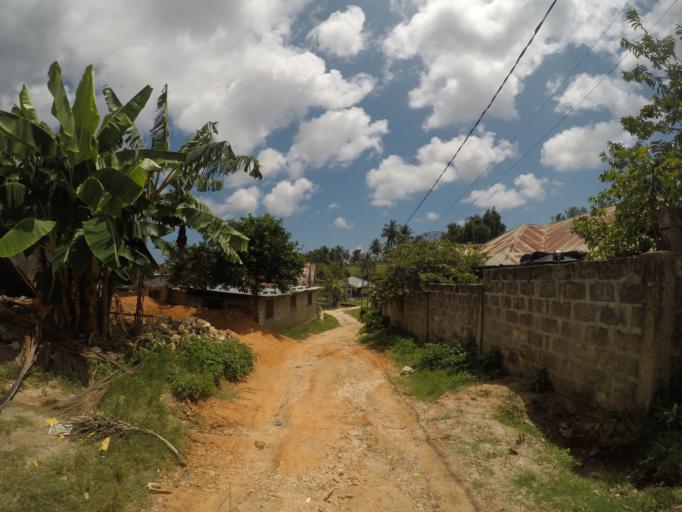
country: TZ
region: Pemba South
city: Chake Chake
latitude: -5.2318
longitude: 39.7813
